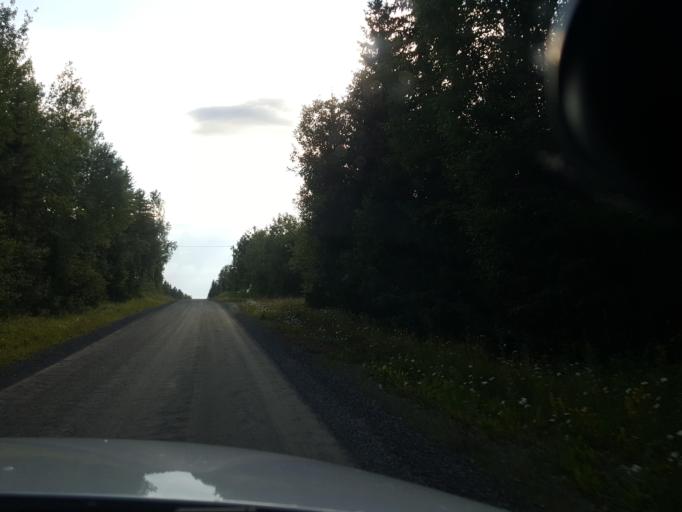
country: SE
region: Vaesternorrland
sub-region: Ange Kommun
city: Ange
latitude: 62.3274
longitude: 15.8174
